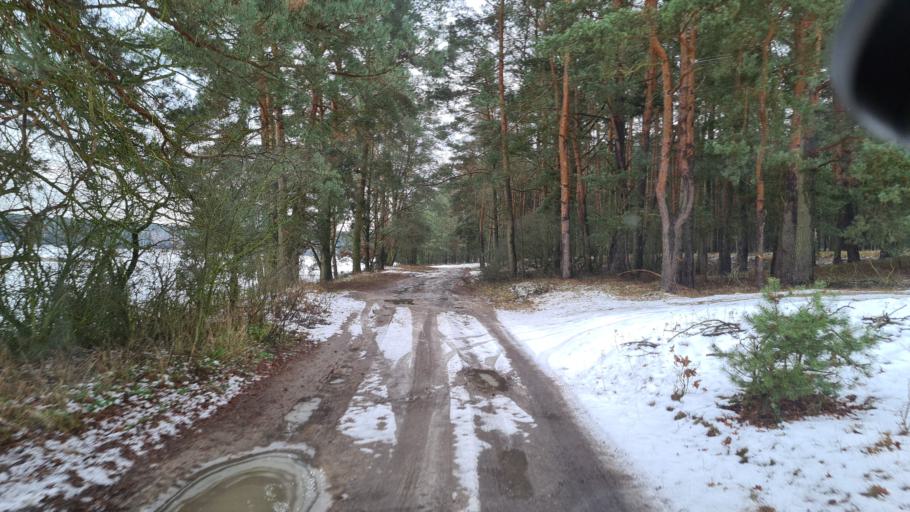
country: DE
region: Brandenburg
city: Schenkendobern
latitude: 51.9035
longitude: 14.5857
